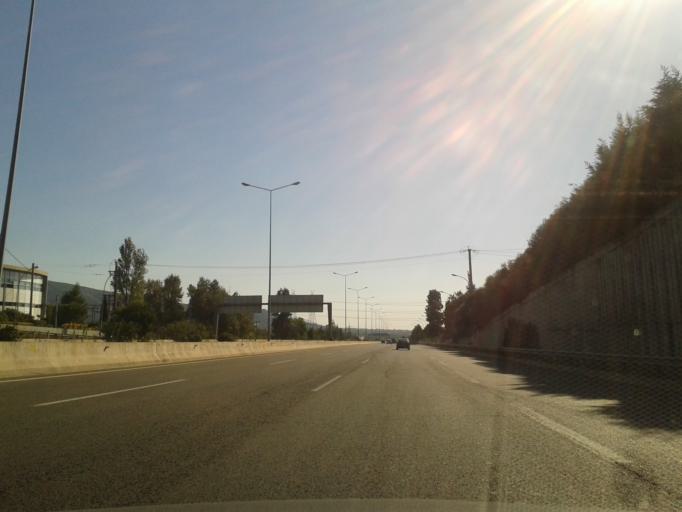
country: GR
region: Attica
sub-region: Nomarchia Anatolikis Attikis
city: Kryoneri
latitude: 38.1373
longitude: 23.8421
